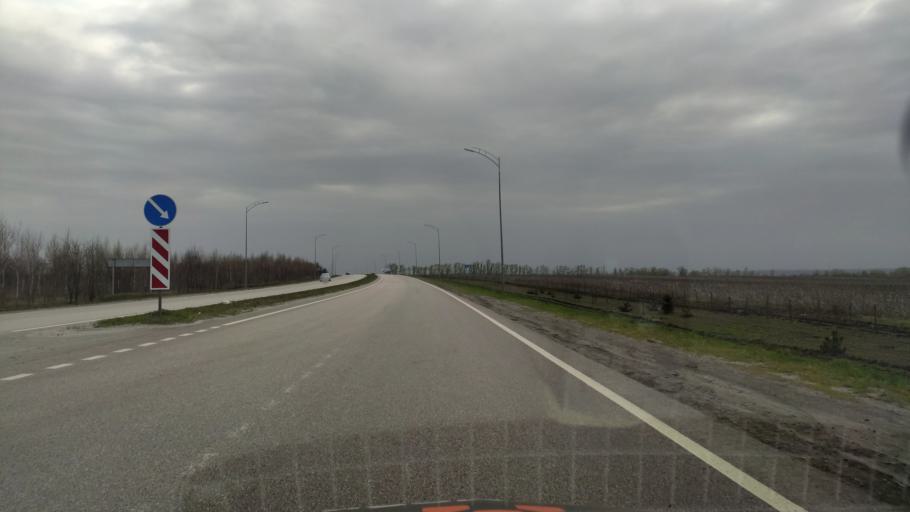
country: RU
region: Belgorod
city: Staryy Oskol
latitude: 51.3819
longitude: 37.8553
